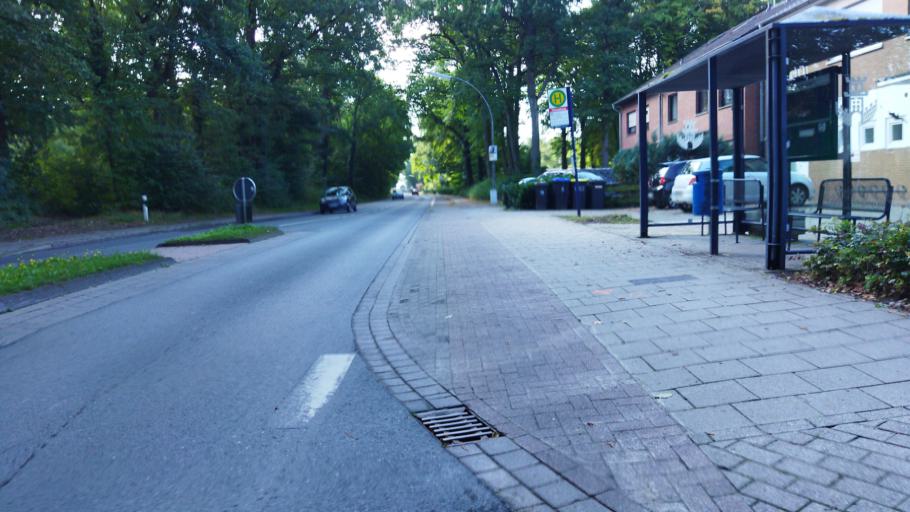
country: DE
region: North Rhine-Westphalia
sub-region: Regierungsbezirk Munster
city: Warendorf
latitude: 51.9715
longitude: 7.9936
